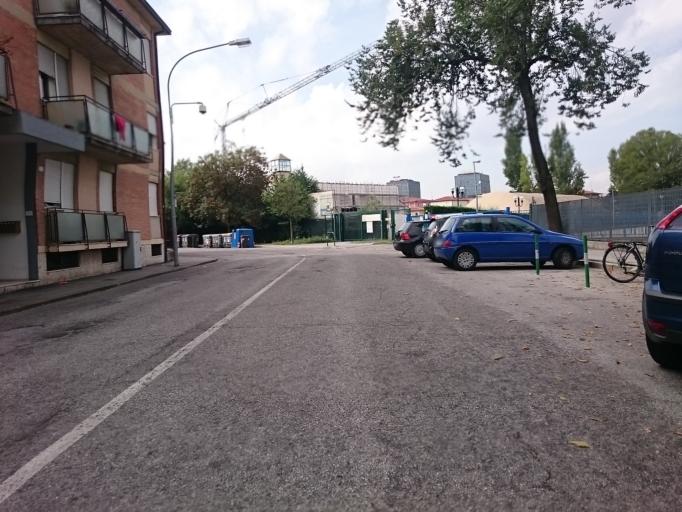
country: IT
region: Veneto
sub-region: Provincia di Padova
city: Padova
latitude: 45.4127
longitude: 11.9062
